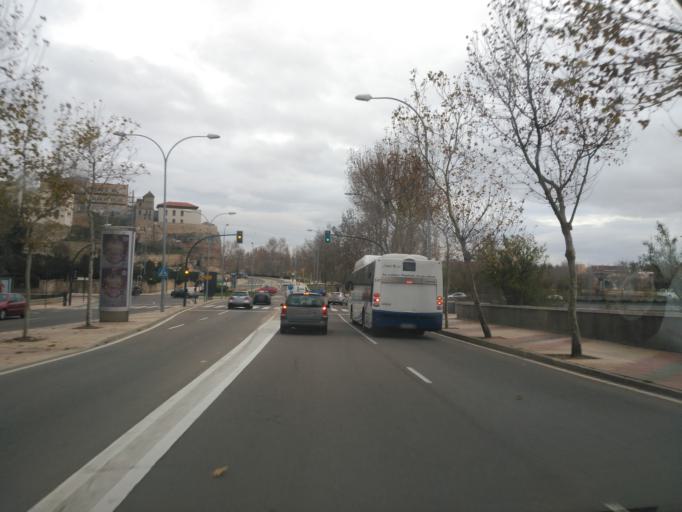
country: ES
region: Castille and Leon
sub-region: Provincia de Salamanca
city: Salamanca
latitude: 40.9608
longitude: -5.6742
